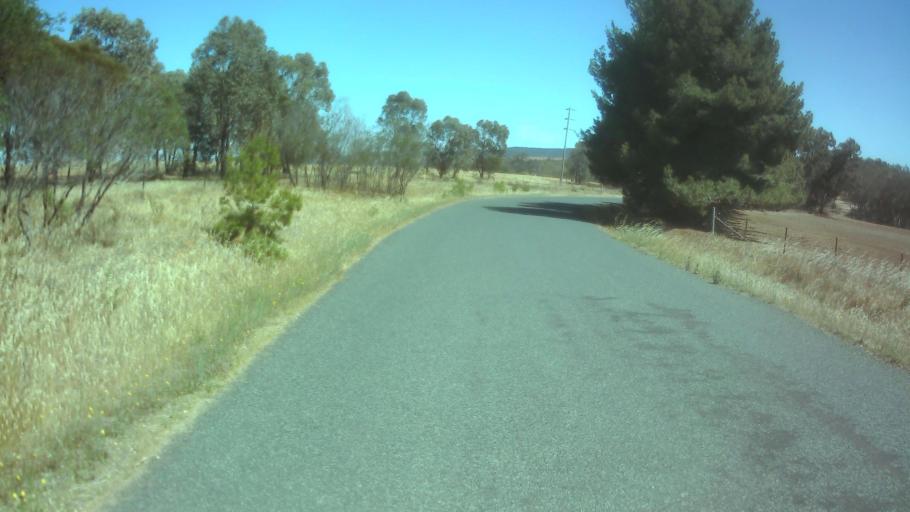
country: AU
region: New South Wales
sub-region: Weddin
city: Grenfell
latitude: -33.9413
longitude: 148.3857
